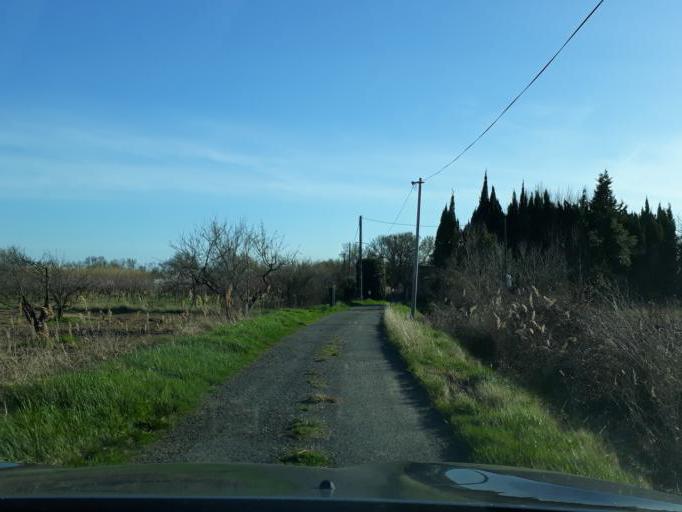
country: FR
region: Languedoc-Roussillon
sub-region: Departement de l'Herault
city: Agde
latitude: 43.3218
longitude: 3.4530
